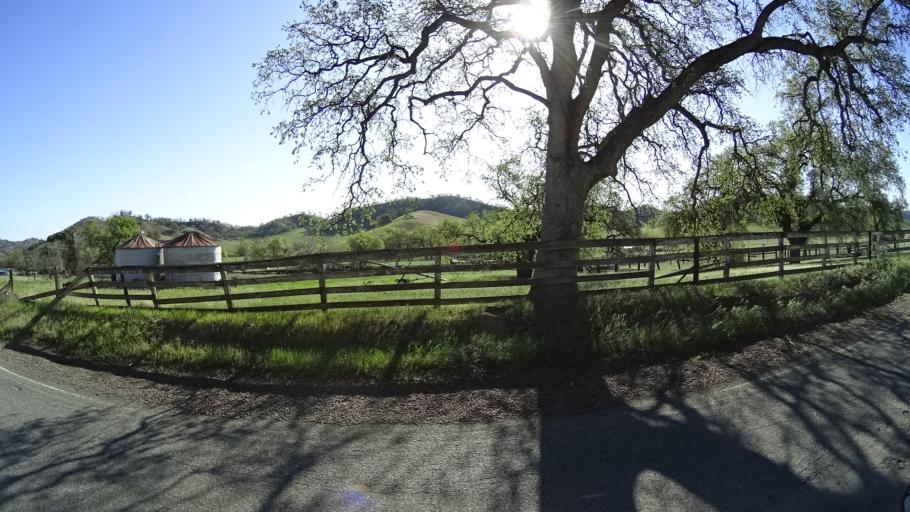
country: US
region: California
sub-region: Tehama County
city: Rancho Tehama Reserve
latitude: 39.7728
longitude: -122.5221
